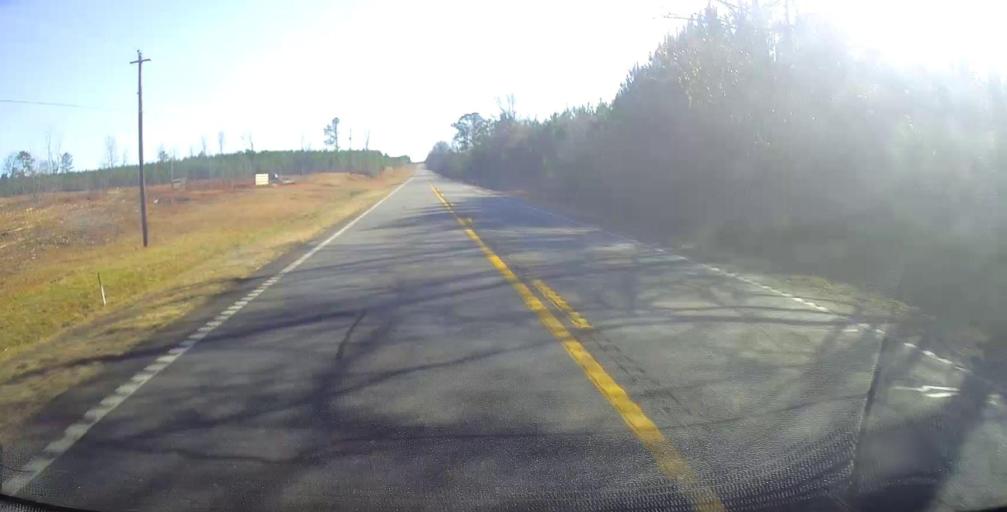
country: US
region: Georgia
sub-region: Talbot County
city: Talbotton
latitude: 32.7314
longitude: -84.5548
